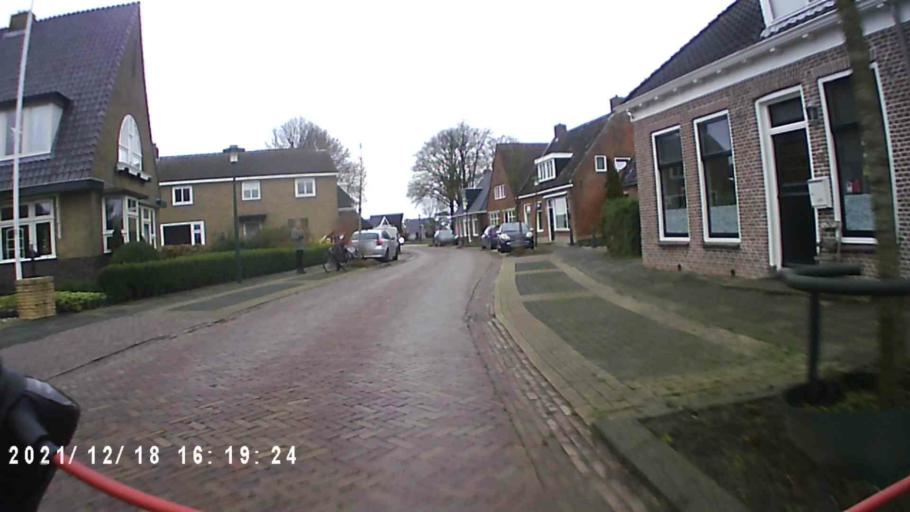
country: NL
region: Friesland
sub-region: Gemeente Dongeradeel
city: Anjum
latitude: 53.3781
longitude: 6.0543
